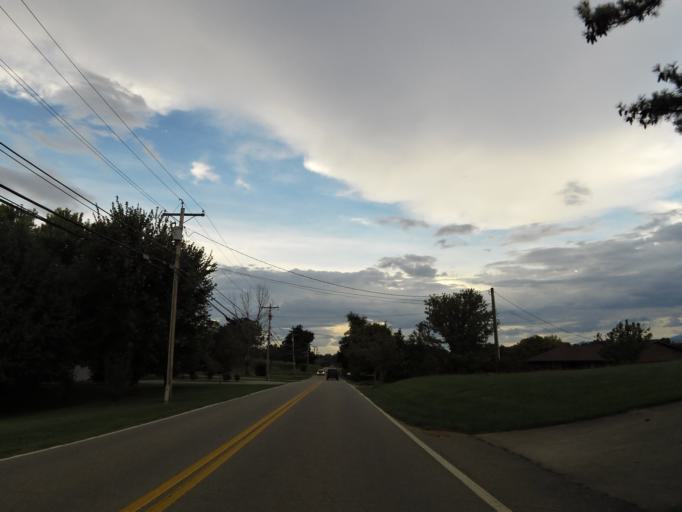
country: US
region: Tennessee
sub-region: Blount County
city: Alcoa
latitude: 35.7823
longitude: -84.0208
